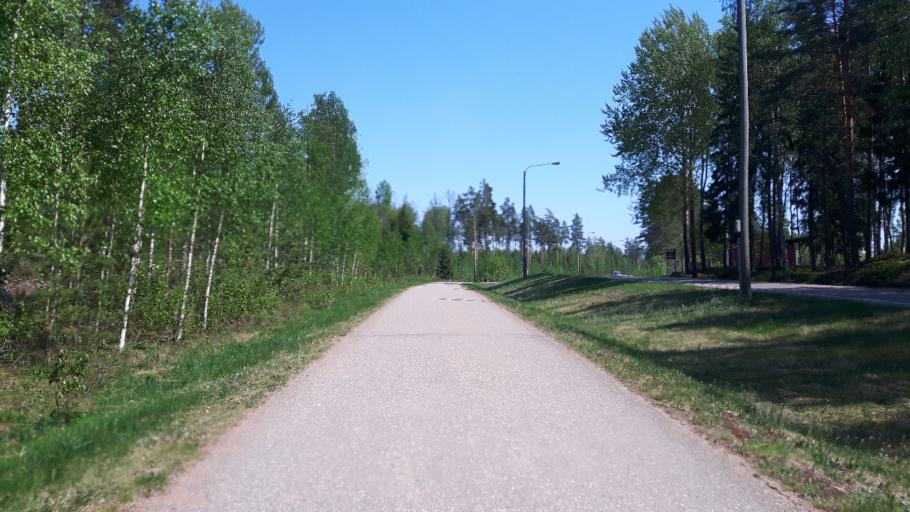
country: FI
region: Kymenlaakso
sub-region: Kotka-Hamina
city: Pyhtaeae
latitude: 60.4909
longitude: 26.5527
